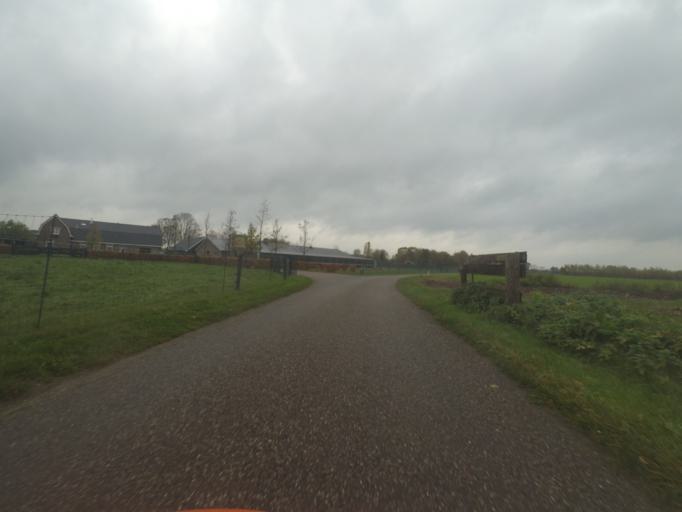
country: NL
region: Gelderland
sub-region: Gemeente Ede
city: Ederveen
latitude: 52.0827
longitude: 5.5667
